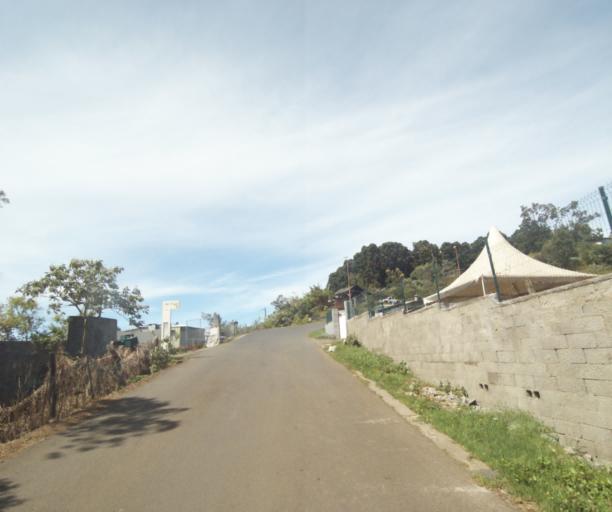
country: RE
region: Reunion
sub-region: Reunion
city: Trois-Bassins
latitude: -21.0483
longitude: 55.3415
